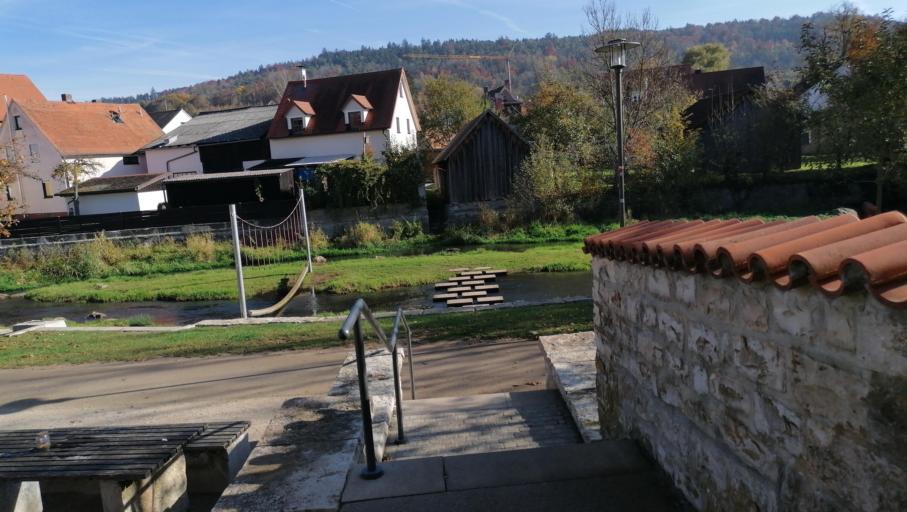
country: DE
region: Bavaria
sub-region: Upper Palatinate
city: Berching
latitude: 49.1052
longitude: 11.4423
